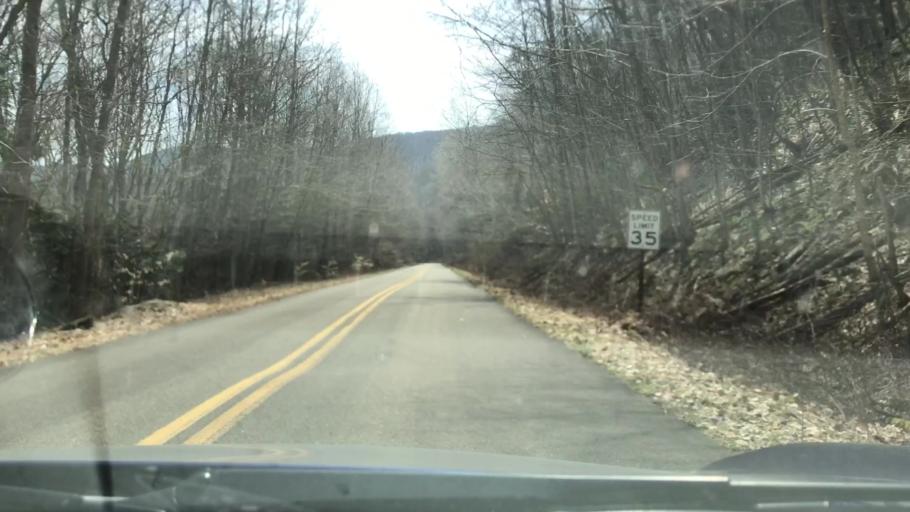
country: US
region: Pennsylvania
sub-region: Warren County
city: Sheffield
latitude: 41.8248
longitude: -78.9555
